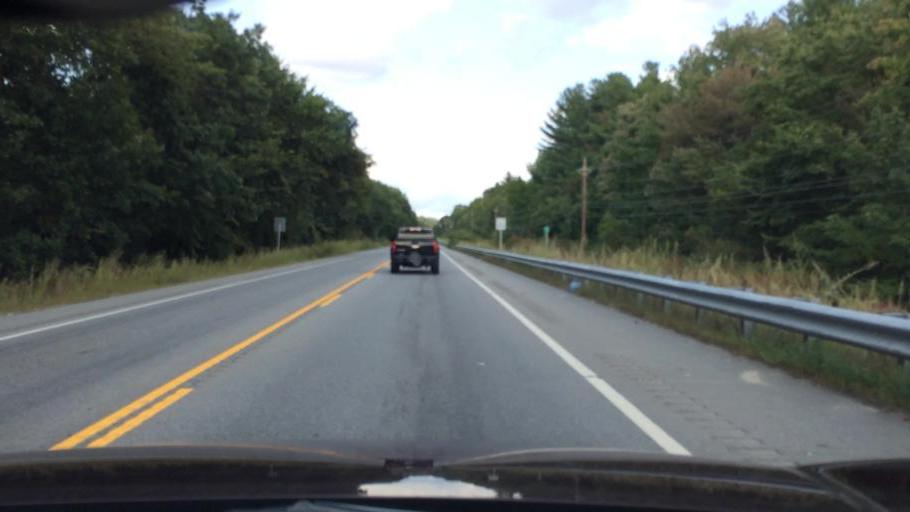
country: US
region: New Hampshire
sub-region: Hillsborough County
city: Hudson
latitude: 42.7731
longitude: -71.4048
